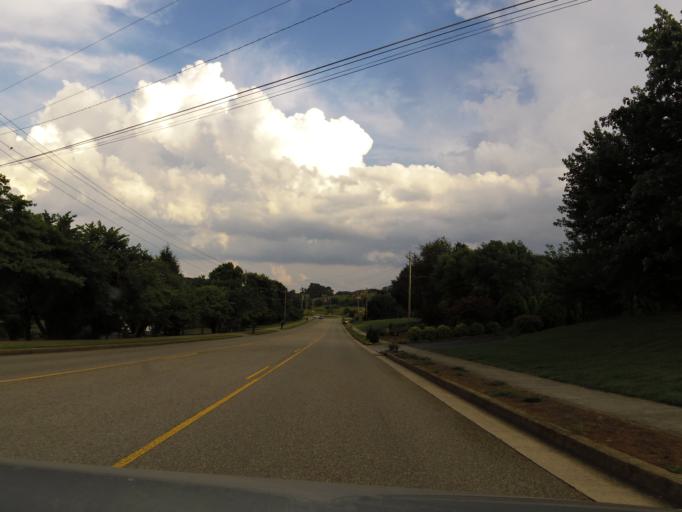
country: US
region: Tennessee
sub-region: Knox County
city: Farragut
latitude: 35.8597
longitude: -84.2000
